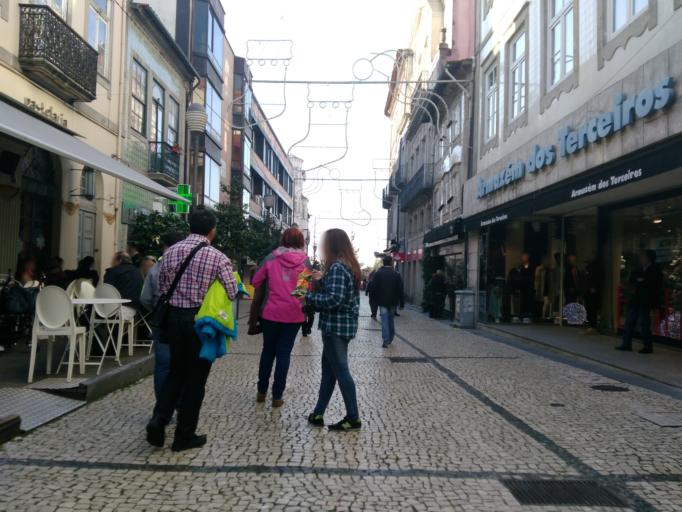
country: PT
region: Braga
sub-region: Braga
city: Braga
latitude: 41.5518
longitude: -8.4248
